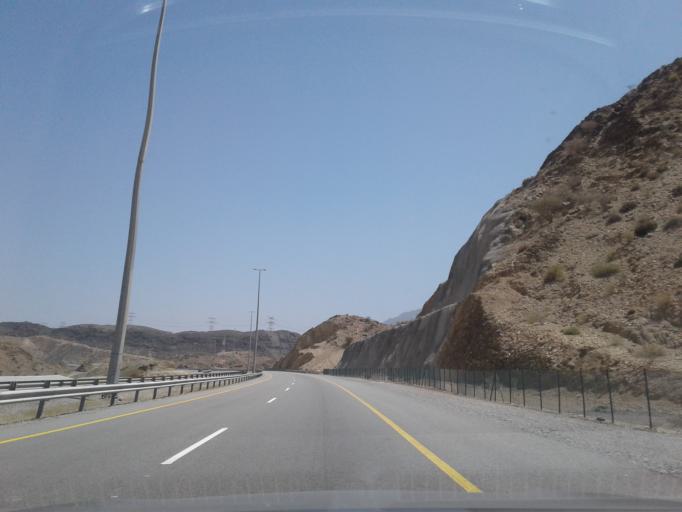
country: OM
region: Muhafazat Masqat
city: Muscat
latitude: 23.2161
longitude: 58.7953
